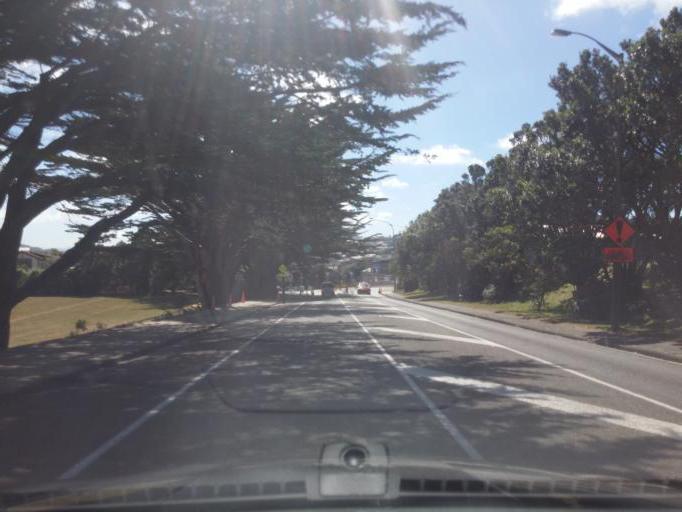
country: NZ
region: Wellington
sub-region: Wellington City
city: Wellington
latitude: -41.2300
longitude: 174.7993
